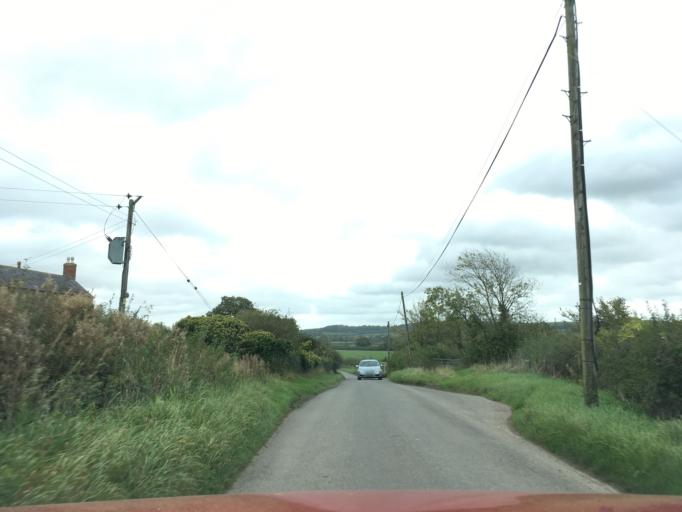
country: GB
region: England
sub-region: South Gloucestershire
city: Wickwar
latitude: 51.5990
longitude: -2.3800
